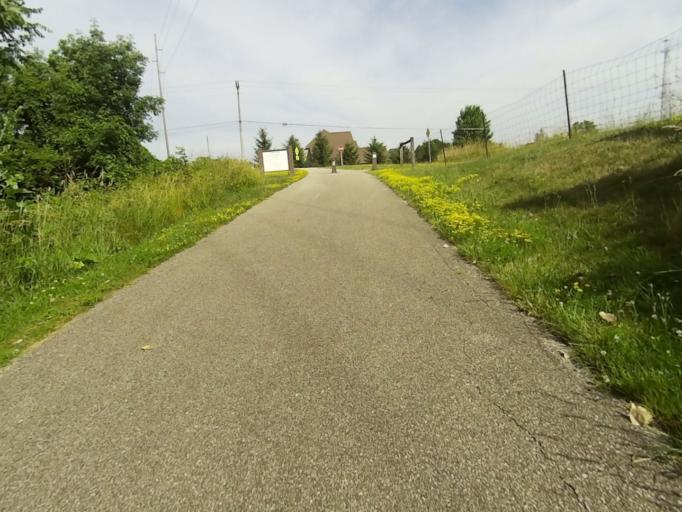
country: US
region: Ohio
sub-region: Summit County
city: Stow
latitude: 41.1942
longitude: -81.4194
